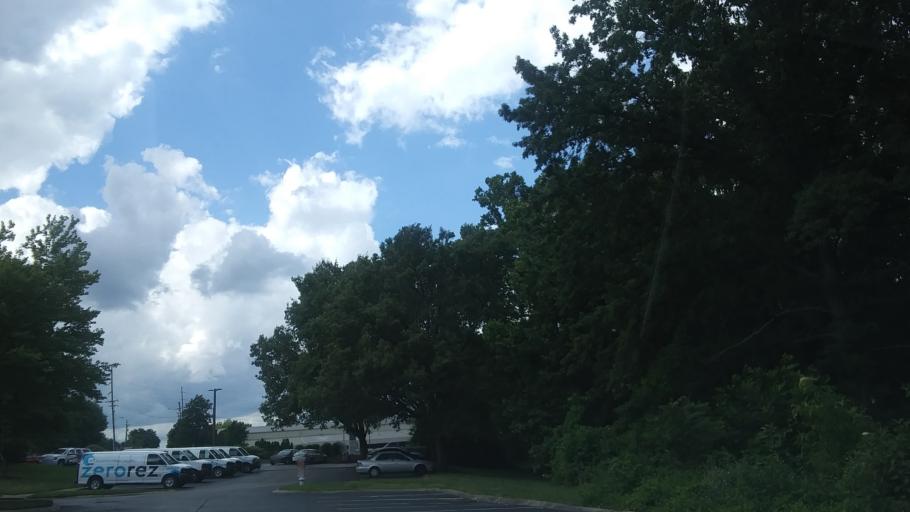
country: US
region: Tennessee
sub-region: Davidson County
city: Oak Hill
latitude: 36.0887
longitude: -86.6994
